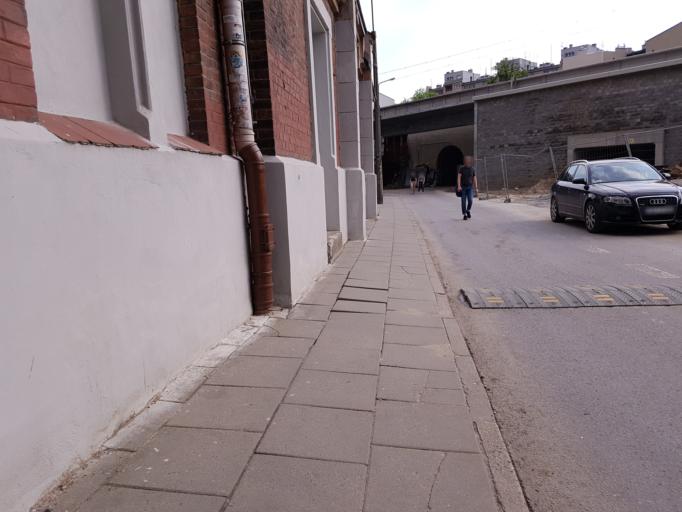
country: PL
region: Lesser Poland Voivodeship
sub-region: Krakow
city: Krakow
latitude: 50.0546
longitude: 19.9502
